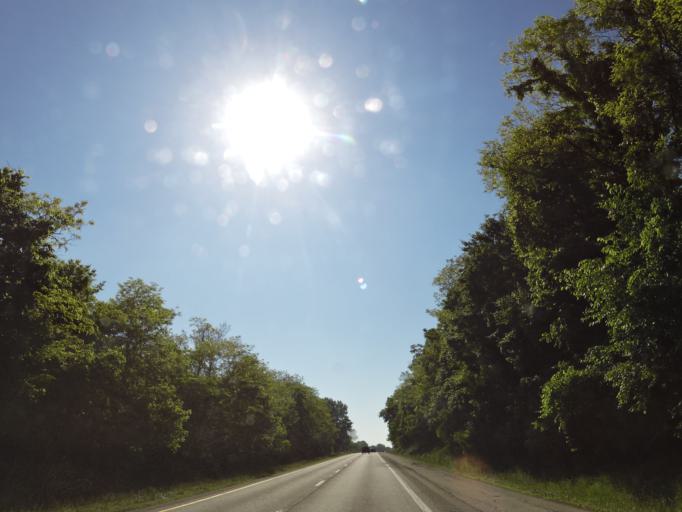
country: US
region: Kentucky
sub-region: Shelby County
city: Shelbyville
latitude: 38.1795
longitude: -85.1773
